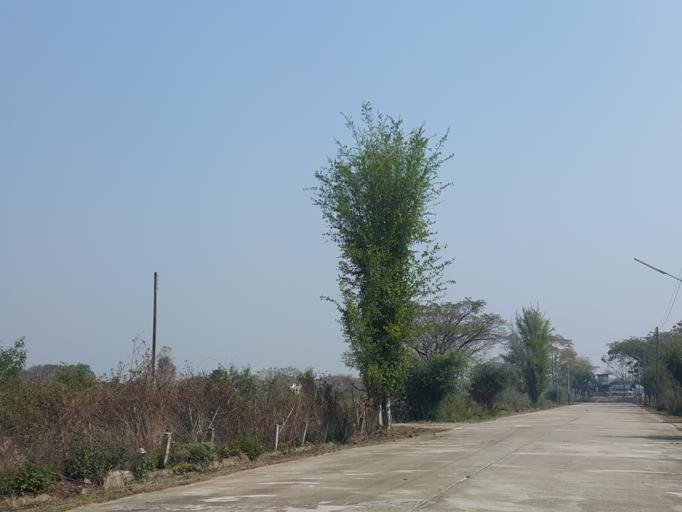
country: TH
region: Chiang Mai
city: San Kamphaeng
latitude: 18.7881
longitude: 99.0786
